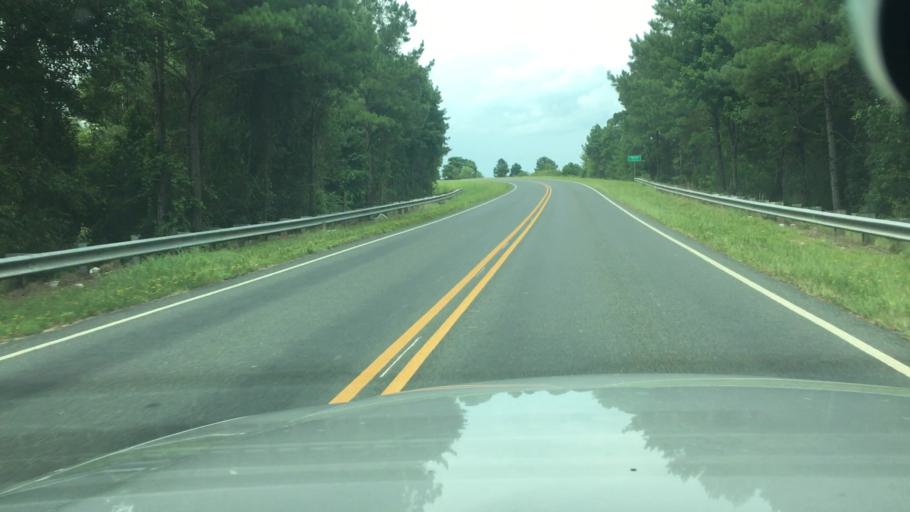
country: US
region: North Carolina
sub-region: Cumberland County
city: Hope Mills
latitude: 34.9802
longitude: -78.8915
